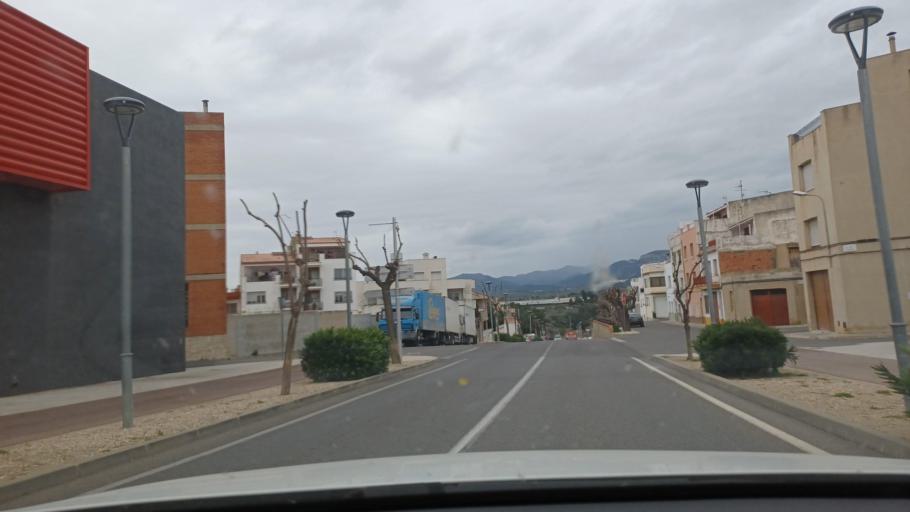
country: ES
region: Valencia
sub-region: Provincia de Castello
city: Rosell
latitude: 40.6331
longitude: 0.2843
